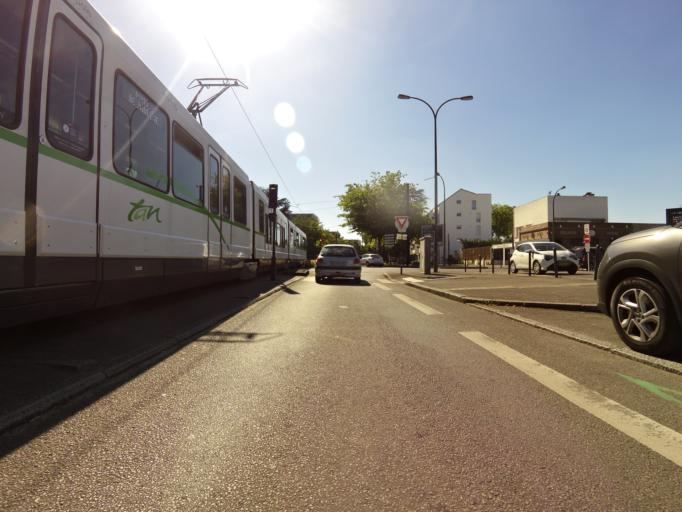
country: FR
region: Pays de la Loire
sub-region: Departement de la Loire-Atlantique
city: Nantes
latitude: 47.2533
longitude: -1.5601
